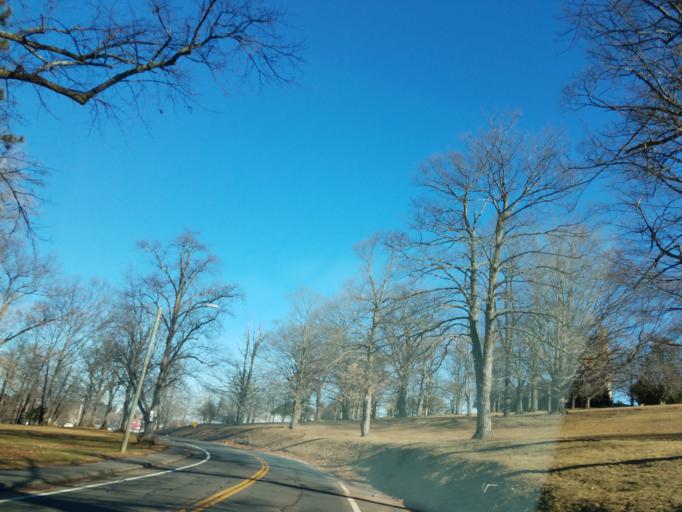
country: US
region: Connecticut
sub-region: Hartford County
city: New Britain
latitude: 41.6643
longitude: -72.7893
